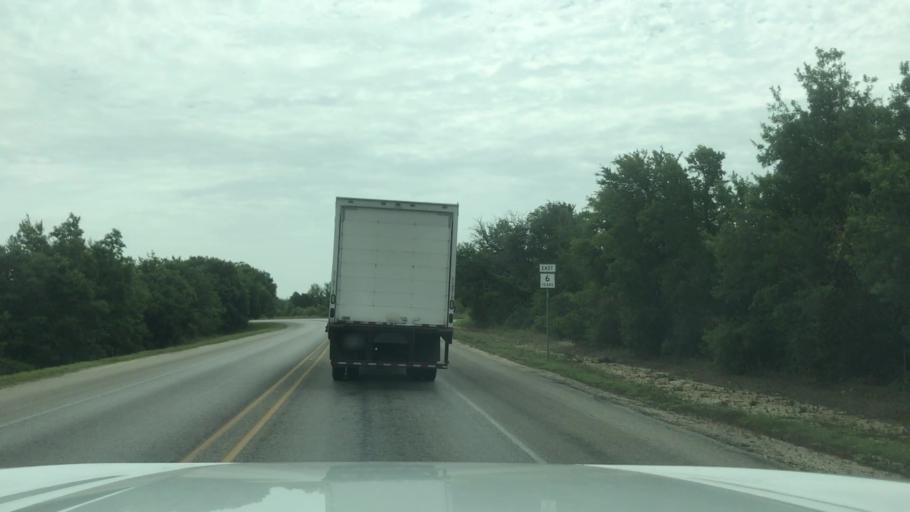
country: US
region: Texas
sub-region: Erath County
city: Dublin
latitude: 32.0885
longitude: -98.4356
